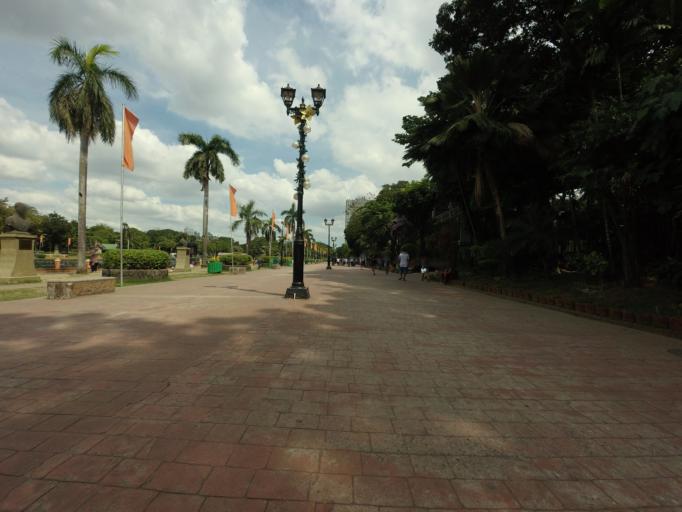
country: PH
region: Metro Manila
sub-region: City of Manila
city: Port Area
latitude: 14.5823
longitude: 120.9788
